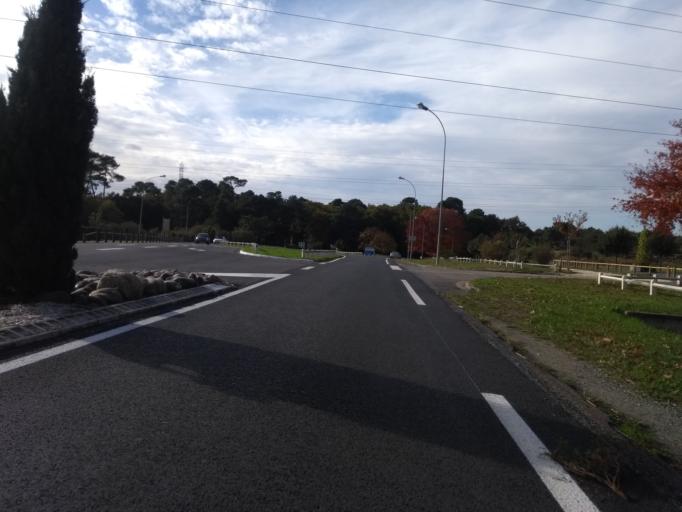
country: FR
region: Aquitaine
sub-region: Departement de la Gironde
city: Cestas
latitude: 44.7655
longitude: -0.6666
